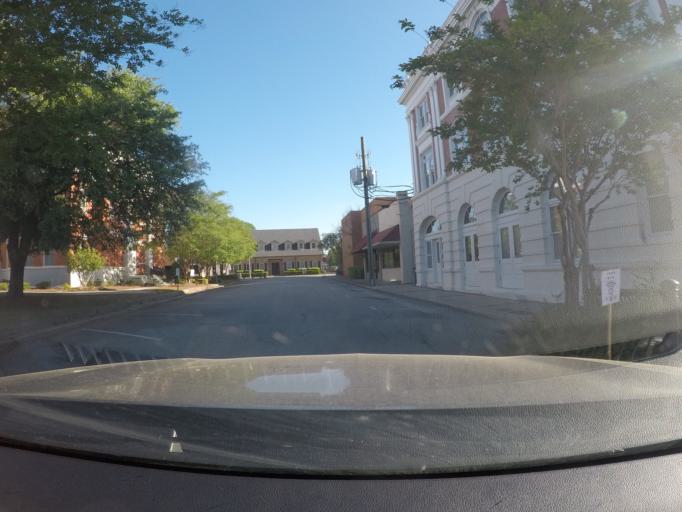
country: US
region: Georgia
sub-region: Bulloch County
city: Statesboro
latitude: 32.4490
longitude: -81.7827
